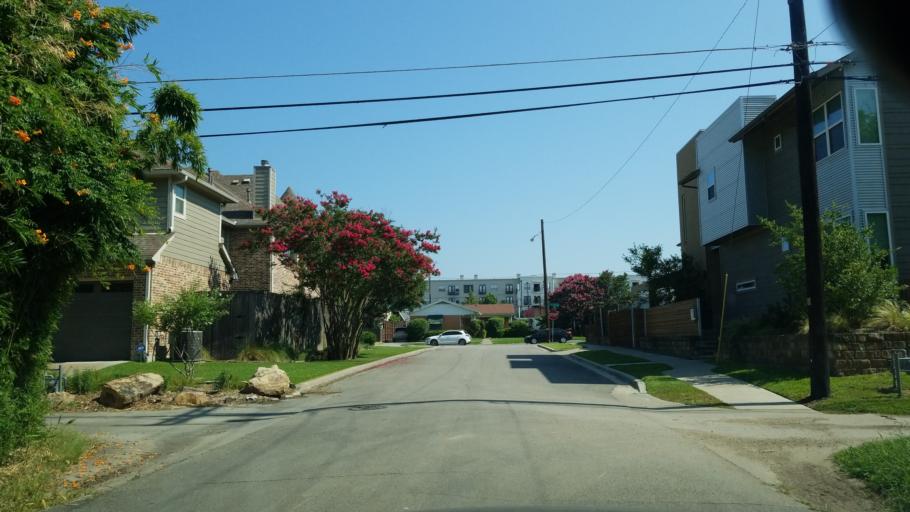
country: US
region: Texas
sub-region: Dallas County
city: Highland Park
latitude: 32.8350
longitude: -96.7722
